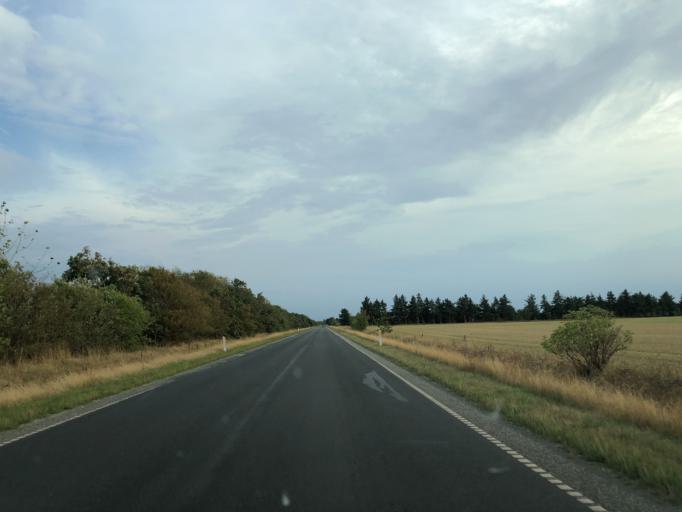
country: DK
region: Central Jutland
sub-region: Holstebro Kommune
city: Holstebro
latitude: 56.3889
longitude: 8.4546
